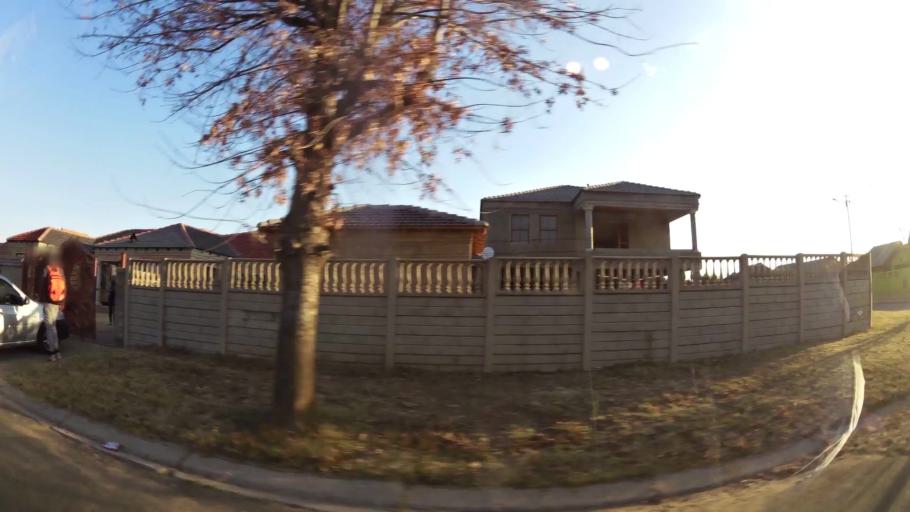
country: ZA
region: Gauteng
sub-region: West Rand District Municipality
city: Randfontein
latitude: -26.2048
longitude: 27.6556
